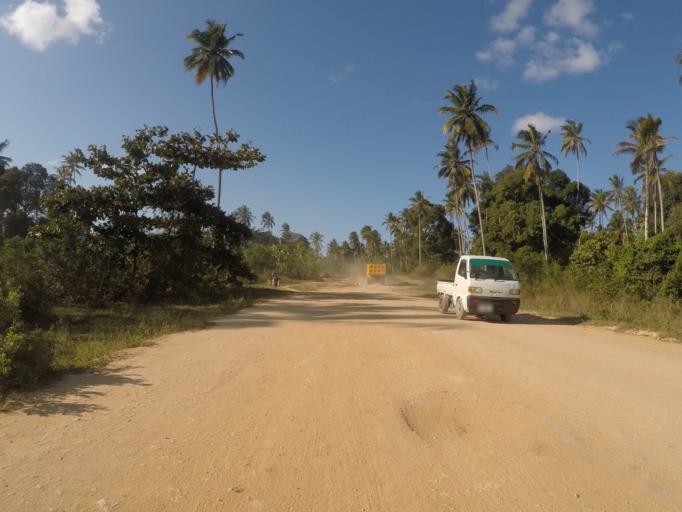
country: TZ
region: Zanzibar Central/South
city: Koani
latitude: -6.1731
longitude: 39.2847
